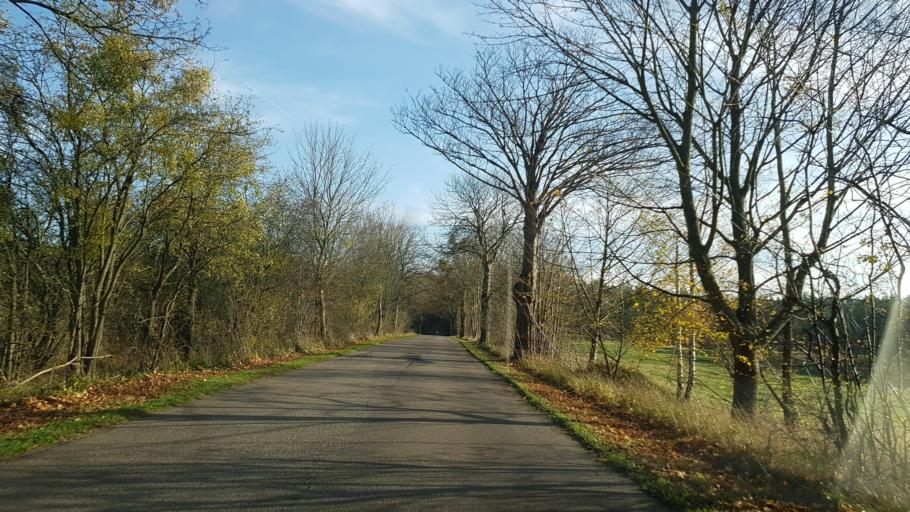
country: PL
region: West Pomeranian Voivodeship
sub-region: Powiat policki
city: Dobra
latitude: 53.5023
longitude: 14.3369
